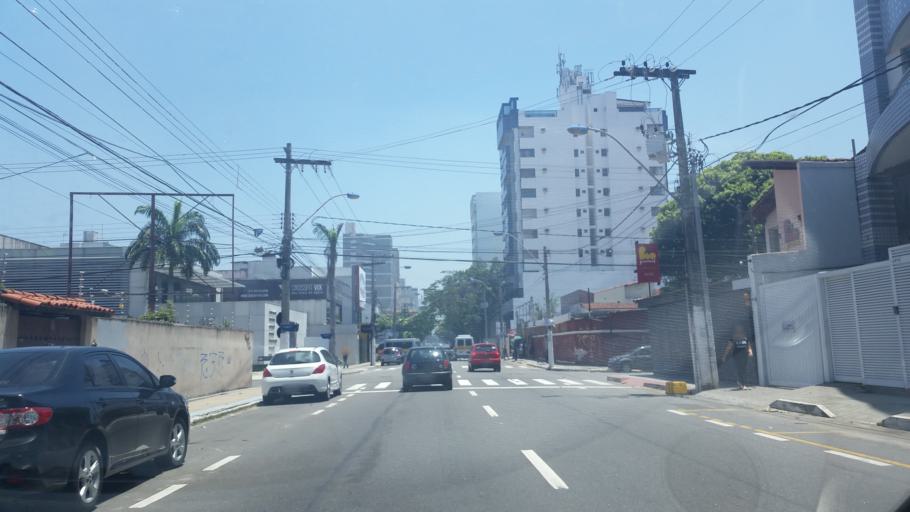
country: BR
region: Espirito Santo
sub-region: Vila Velha
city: Vila Velha
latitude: -20.3361
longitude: -40.2850
